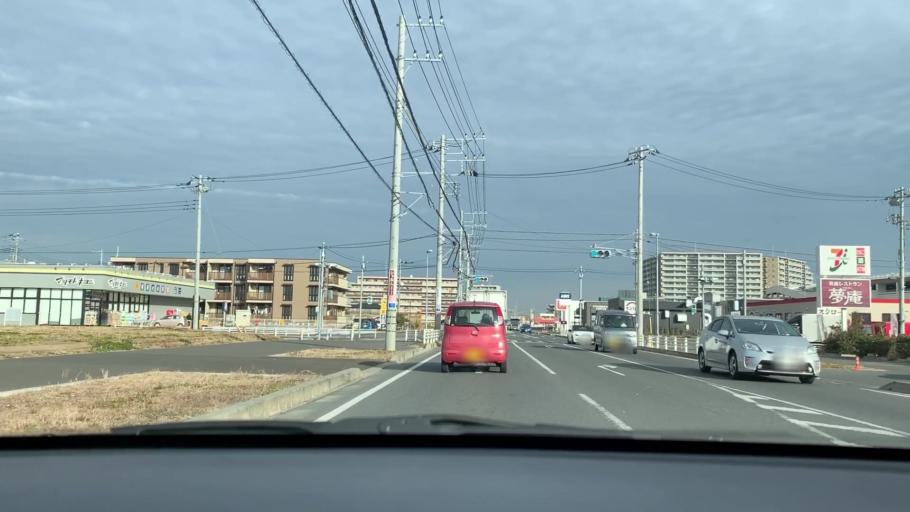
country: JP
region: Chiba
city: Nagareyama
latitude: 35.8308
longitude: 139.8958
